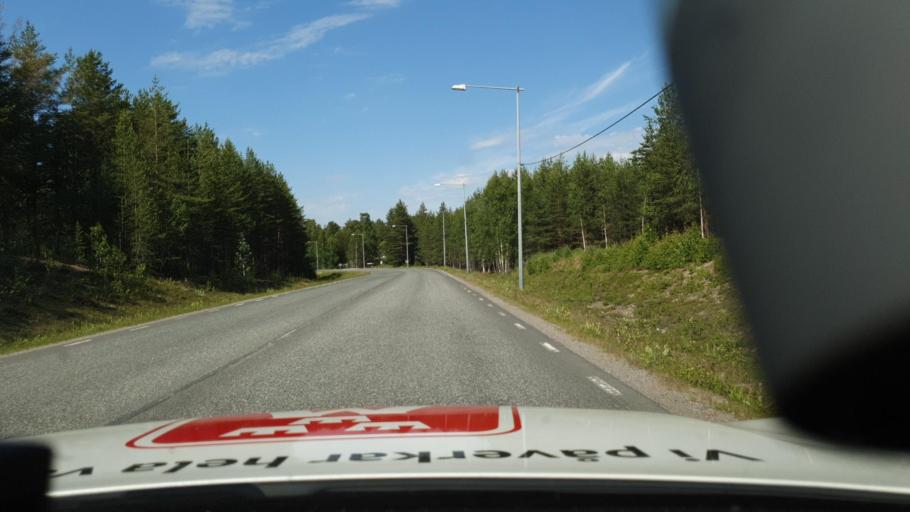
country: SE
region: Norrbotten
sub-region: Kalix Kommun
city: Rolfs
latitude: 65.8663
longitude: 23.1311
